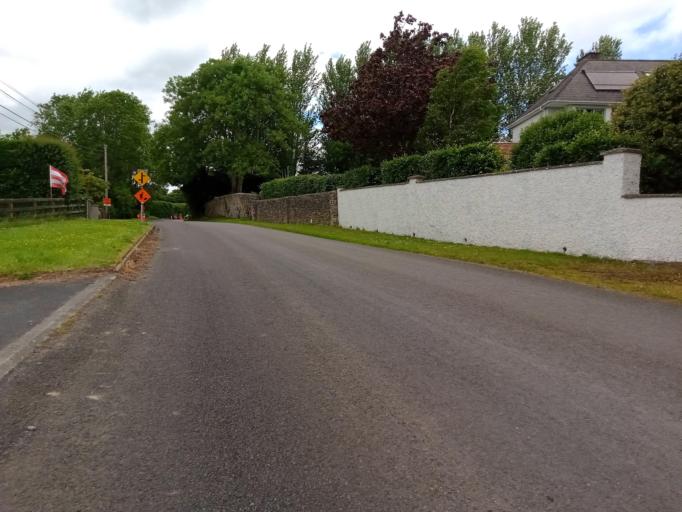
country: IE
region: Leinster
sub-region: Kilkenny
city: Kilkenny
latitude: 52.6841
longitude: -7.2489
